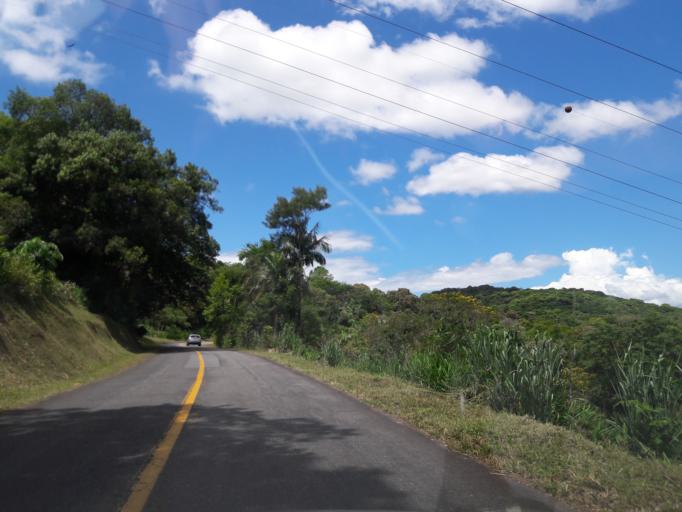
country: BR
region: Parana
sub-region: Antonina
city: Antonina
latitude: -25.4286
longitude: -48.8084
